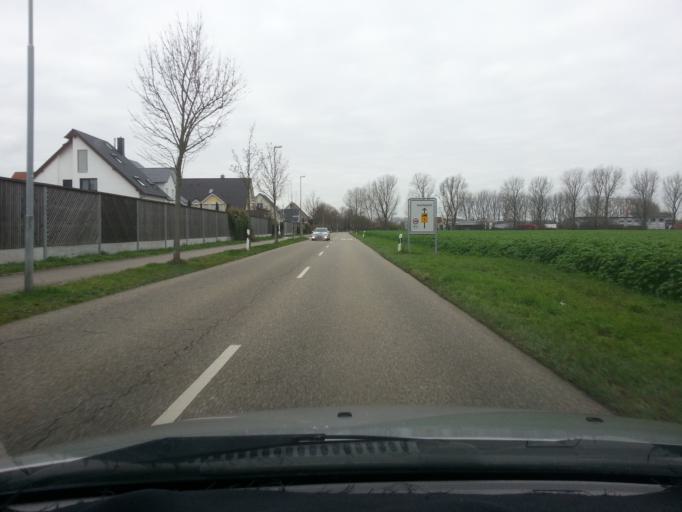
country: DE
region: Baden-Wuerttemberg
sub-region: Karlsruhe Region
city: Reilingen
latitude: 49.3006
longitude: 8.5643
